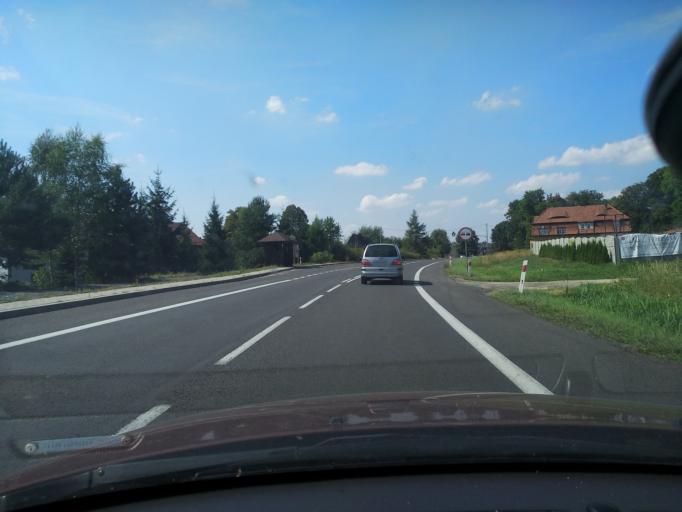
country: PL
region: Lower Silesian Voivodeship
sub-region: Powiat lubanski
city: Olszyna
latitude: 51.0813
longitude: 15.3350
